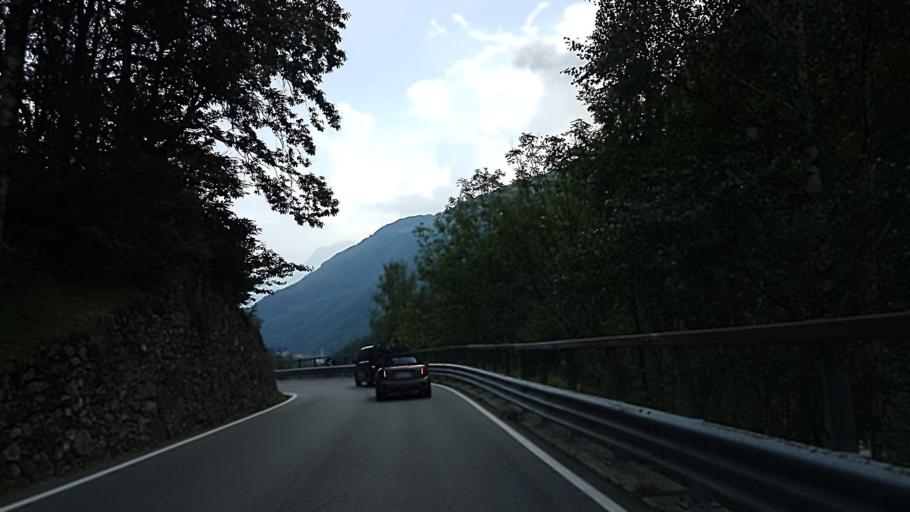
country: IT
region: Lombardy
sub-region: Provincia di Sondrio
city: San Giacomo Filippo
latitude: 46.3539
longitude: 9.3660
